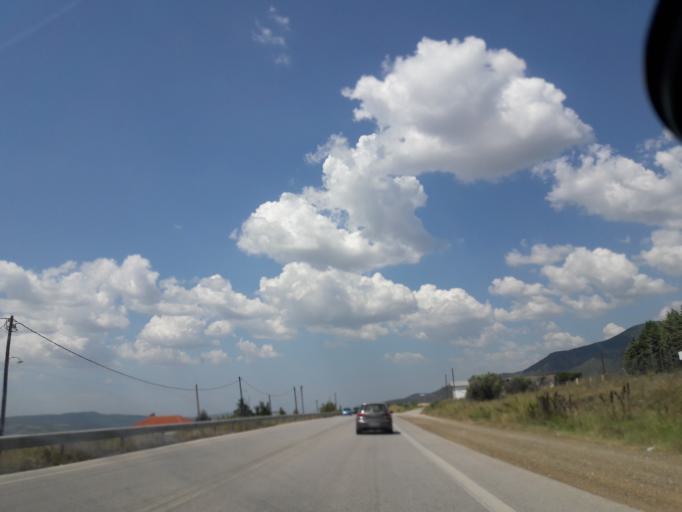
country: GR
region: Central Macedonia
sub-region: Nomos Chalkidikis
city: Galatista
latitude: 40.4632
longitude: 23.2711
